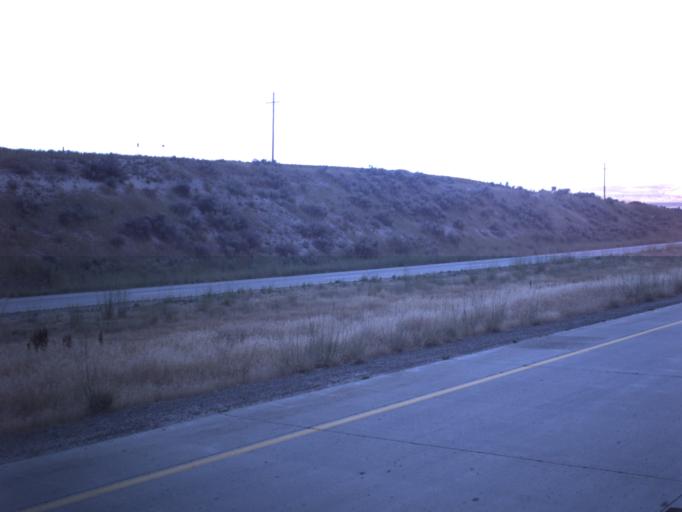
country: US
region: Utah
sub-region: Box Elder County
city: Garland
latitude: 41.8870
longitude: -112.4972
